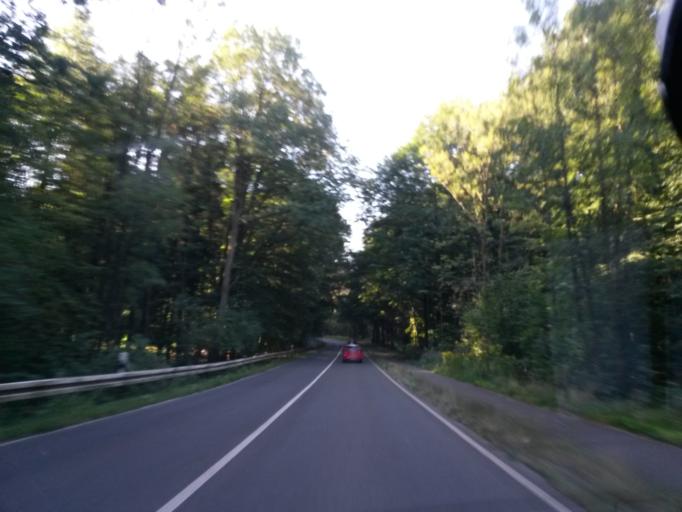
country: DE
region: North Rhine-Westphalia
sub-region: Regierungsbezirk Koln
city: Rosrath
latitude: 50.9376
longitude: 7.1695
